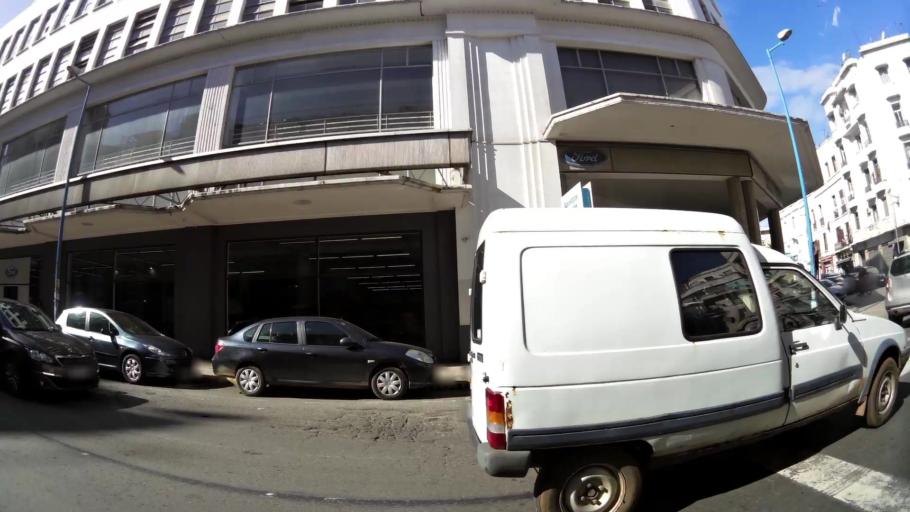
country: MA
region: Grand Casablanca
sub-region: Casablanca
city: Casablanca
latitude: 33.5907
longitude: -7.6130
